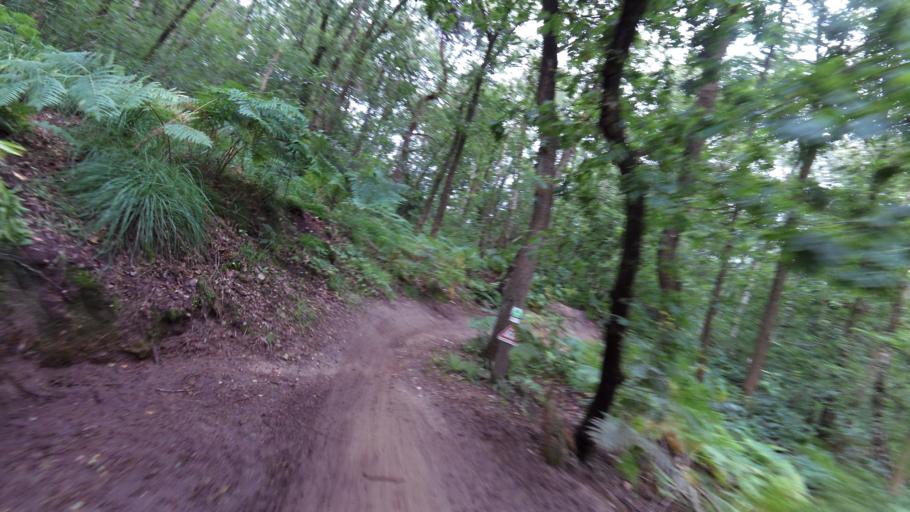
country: NL
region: Utrecht
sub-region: Gemeente Utrechtse Heuvelrug
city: Amerongen
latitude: 52.0076
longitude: 5.4723
